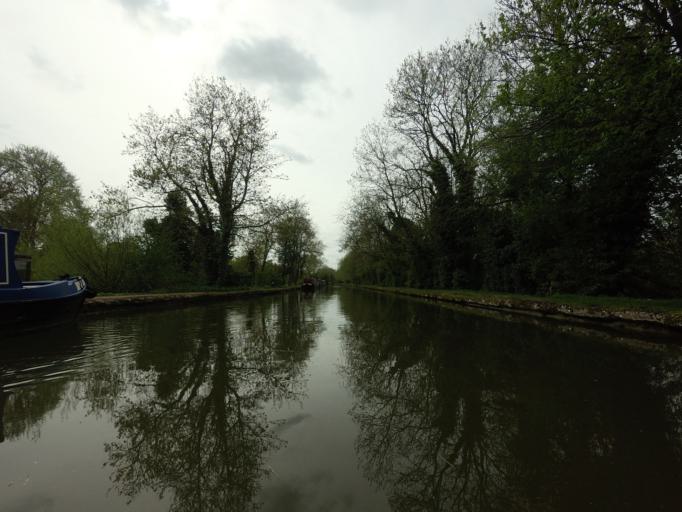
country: GB
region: England
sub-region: Milton Keynes
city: Milton Keynes
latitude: 52.0738
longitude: -0.7588
